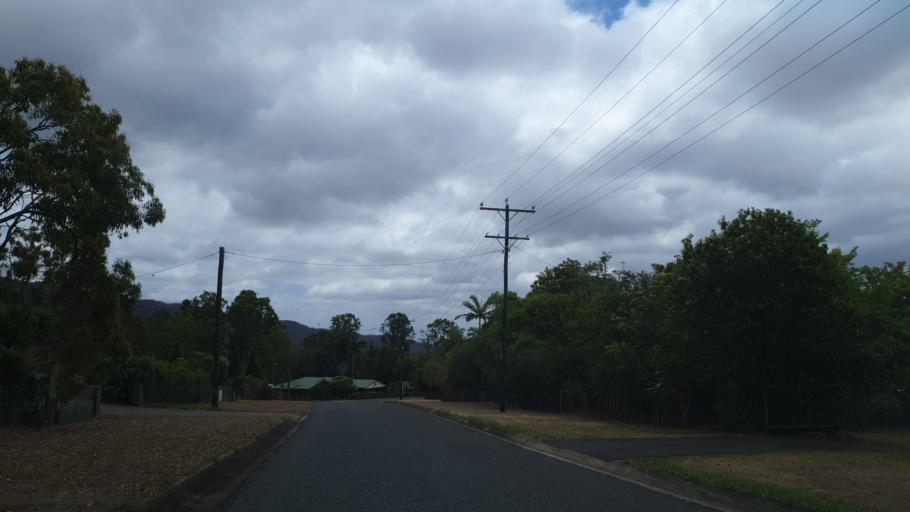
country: AU
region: Queensland
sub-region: Tablelands
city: Tolga
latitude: -17.2097
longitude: 145.4440
